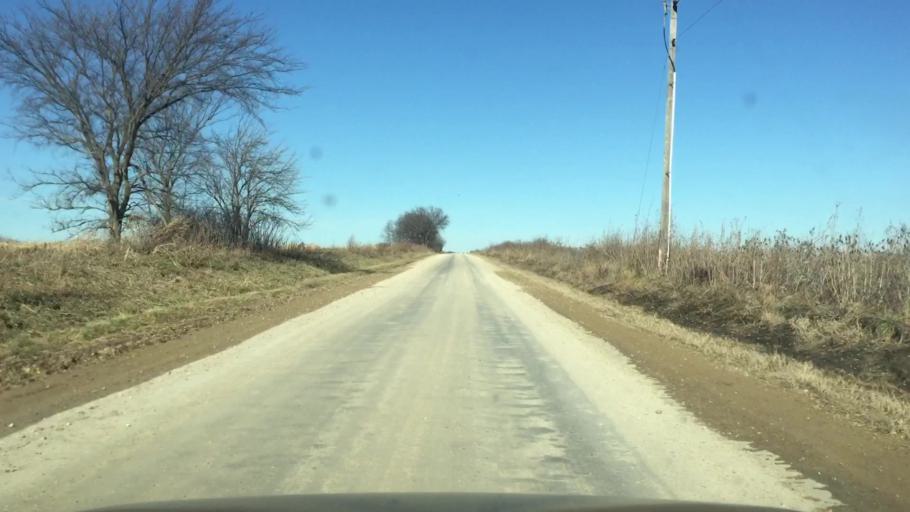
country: US
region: Kansas
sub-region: Allen County
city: Humboldt
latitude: 37.8550
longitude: -95.3910
